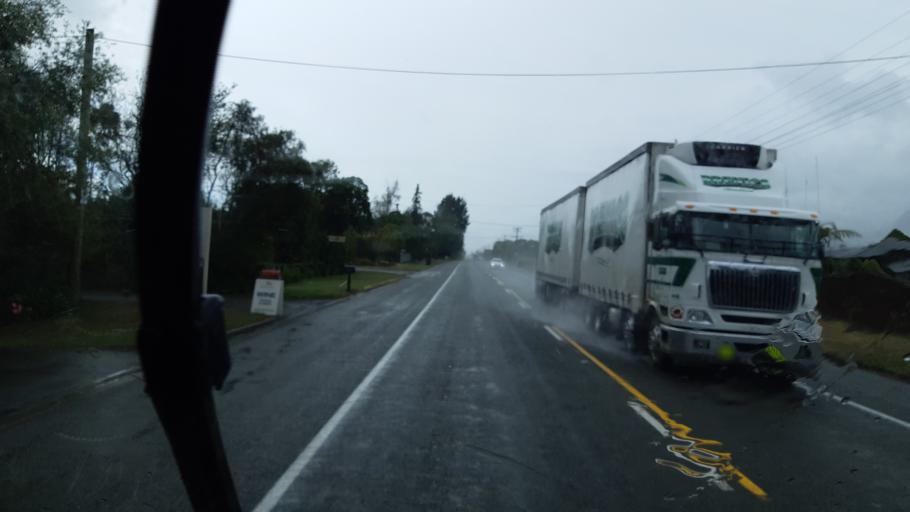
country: NZ
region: Tasman
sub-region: Tasman District
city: Brightwater
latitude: -41.3687
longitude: 173.1306
